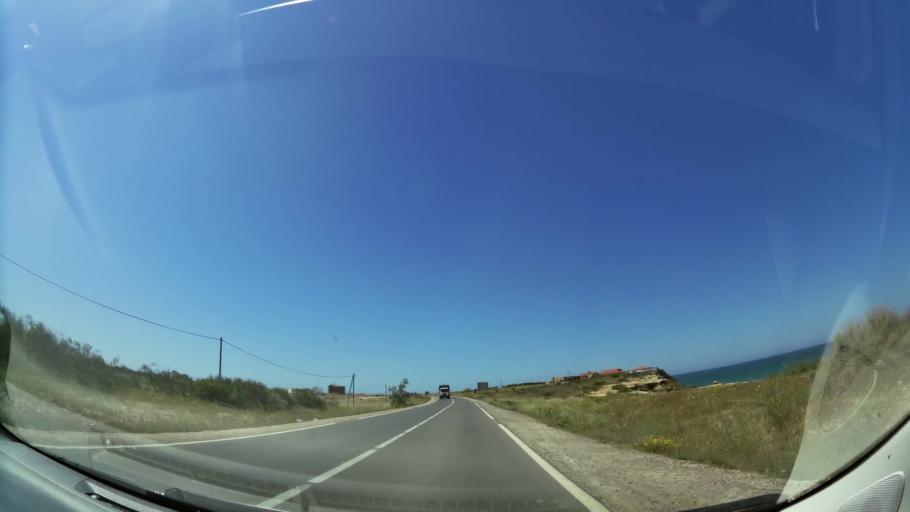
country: MA
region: Oriental
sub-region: Berkane-Taourirt
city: Madagh
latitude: 35.1295
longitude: -2.3962
